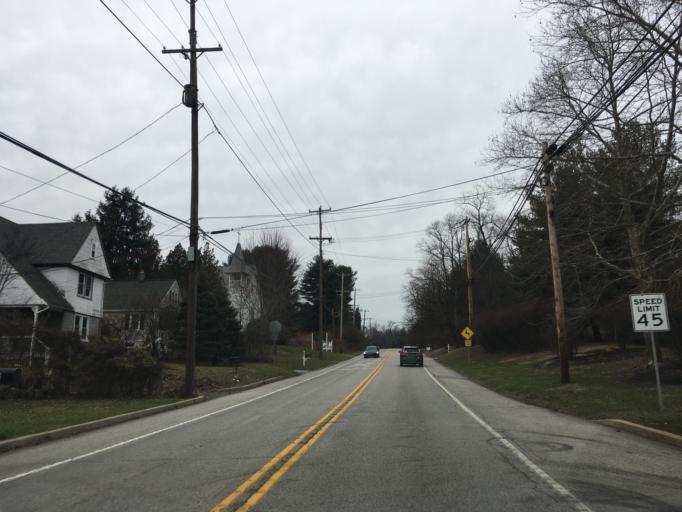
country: US
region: Pennsylvania
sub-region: Chester County
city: Kennett Square
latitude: 39.8544
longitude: -75.6416
